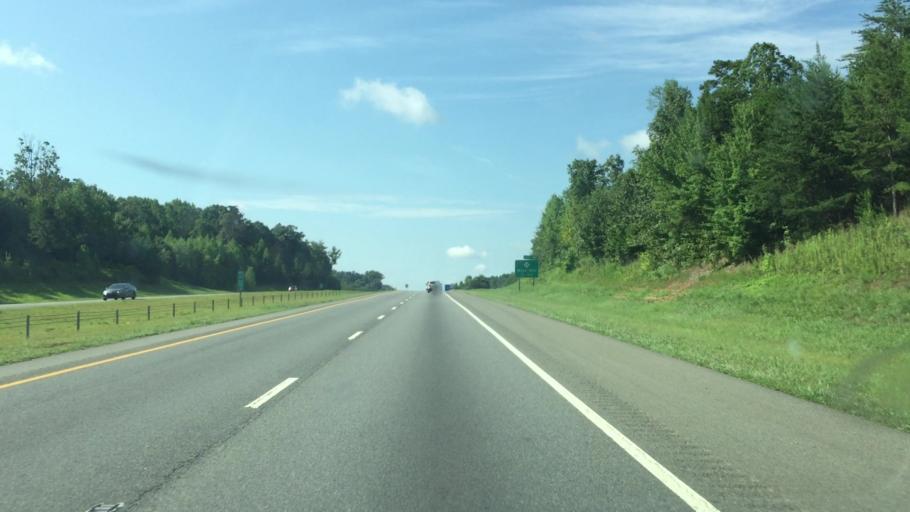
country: US
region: North Carolina
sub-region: Mecklenburg County
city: Mint Hill
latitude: 35.1917
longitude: -80.6295
